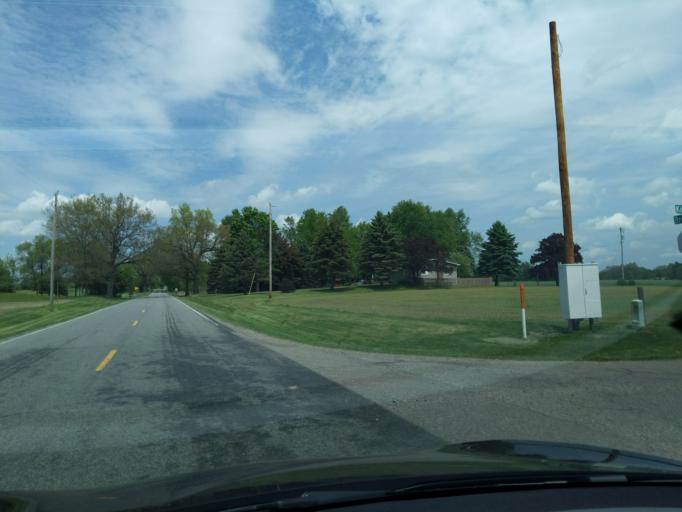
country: US
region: Michigan
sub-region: Ingham County
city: Stockbridge
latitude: 42.5047
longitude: -84.1600
